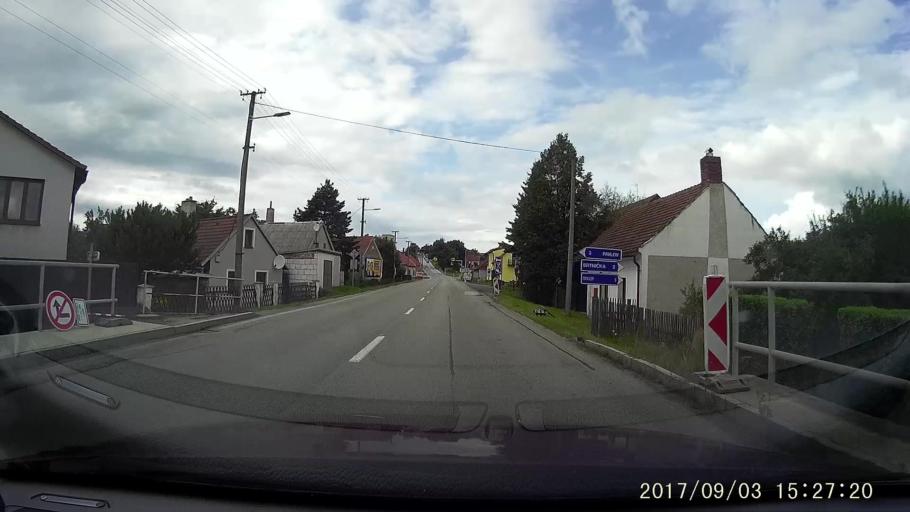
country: CZ
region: Vysocina
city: Knezice
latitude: 49.2362
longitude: 15.6052
